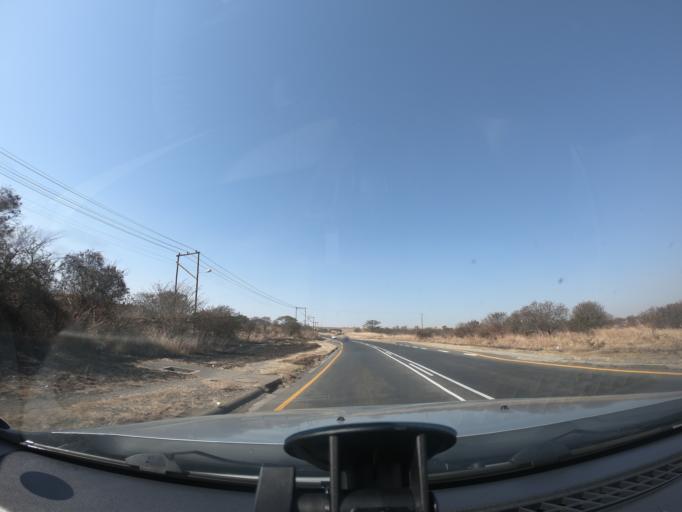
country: ZA
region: KwaZulu-Natal
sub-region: uThukela District Municipality
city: Ladysmith
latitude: -28.5421
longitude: 29.8063
